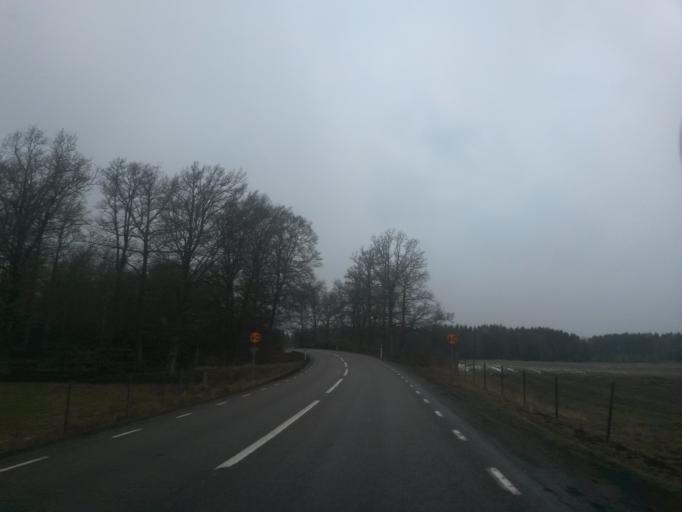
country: SE
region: Vaestra Goetaland
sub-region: Alingsas Kommun
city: Sollebrunn
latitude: 58.1615
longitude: 12.4249
